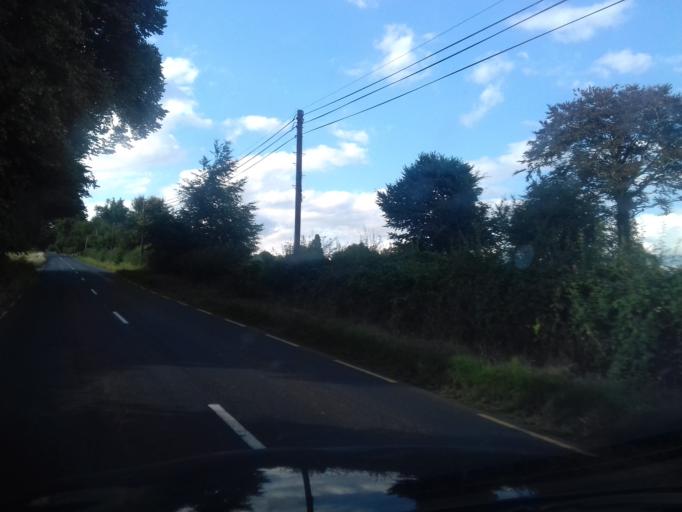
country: IE
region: Leinster
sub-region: Loch Garman
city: New Ross
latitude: 52.4420
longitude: -6.9607
